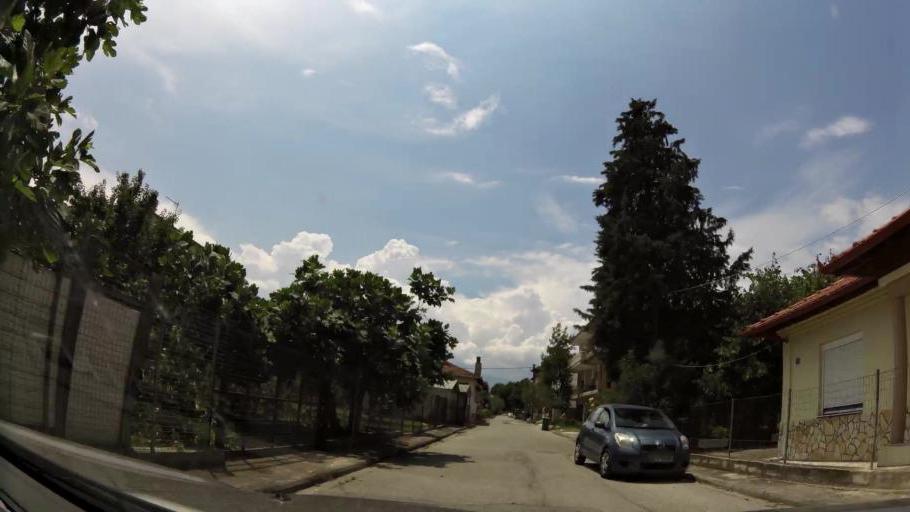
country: GR
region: Central Macedonia
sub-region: Nomos Pierias
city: Peristasi
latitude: 40.2759
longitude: 22.5387
